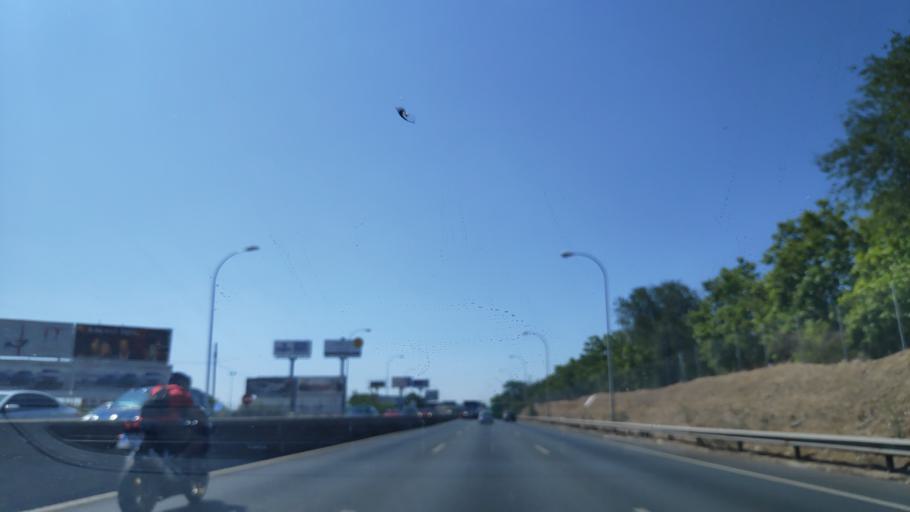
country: ES
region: Madrid
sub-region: Provincia de Madrid
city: Getafe
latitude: 40.2905
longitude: -3.7411
